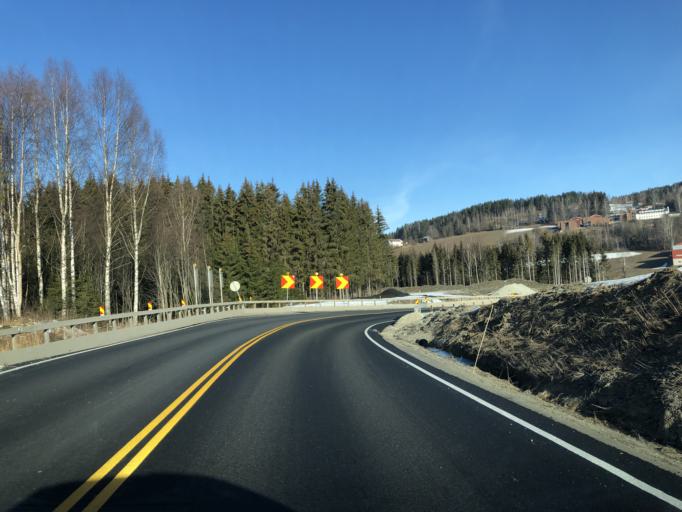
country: NO
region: Hedmark
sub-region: Ringsaker
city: Moelv
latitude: 60.9074
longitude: 10.7355
